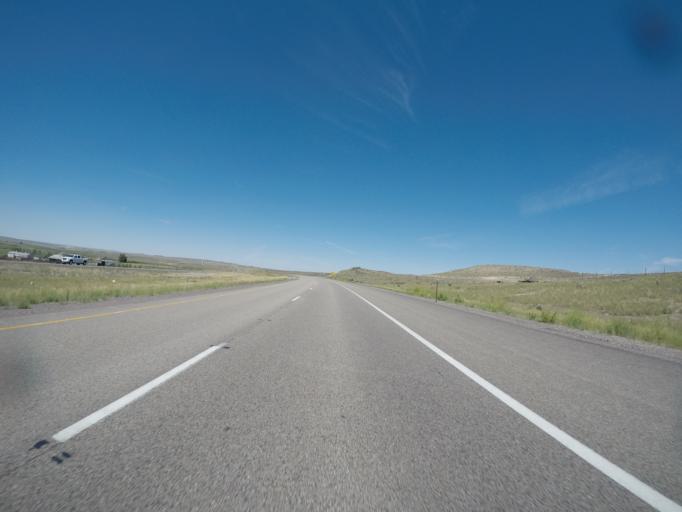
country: US
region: Wyoming
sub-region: Carbon County
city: Saratoga
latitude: 41.7429
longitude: -106.7678
